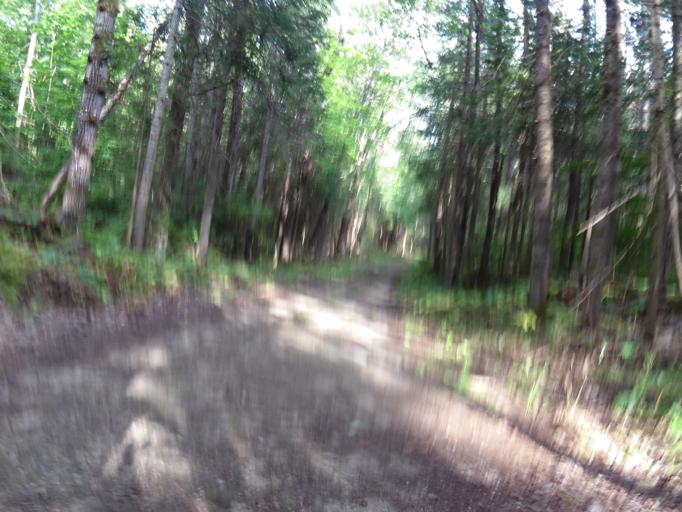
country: CA
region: Quebec
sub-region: Outaouais
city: Wakefield
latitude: 45.6283
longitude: -75.9777
